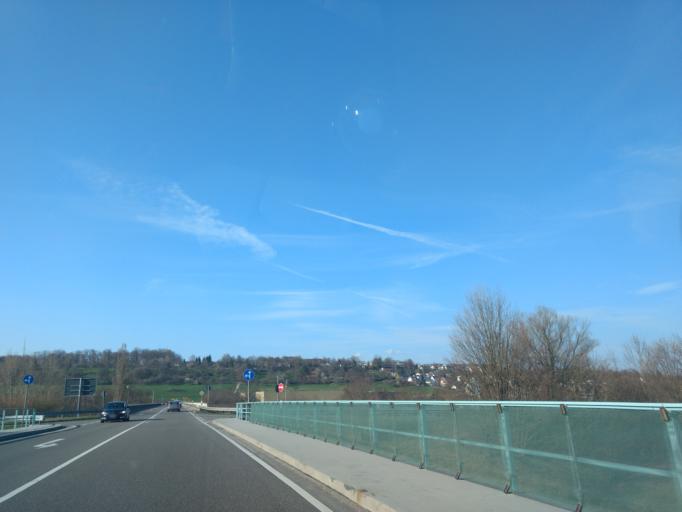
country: DE
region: Baden-Wuerttemberg
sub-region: Regierungsbezirk Stuttgart
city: Uhingen
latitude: 48.7037
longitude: 9.6071
